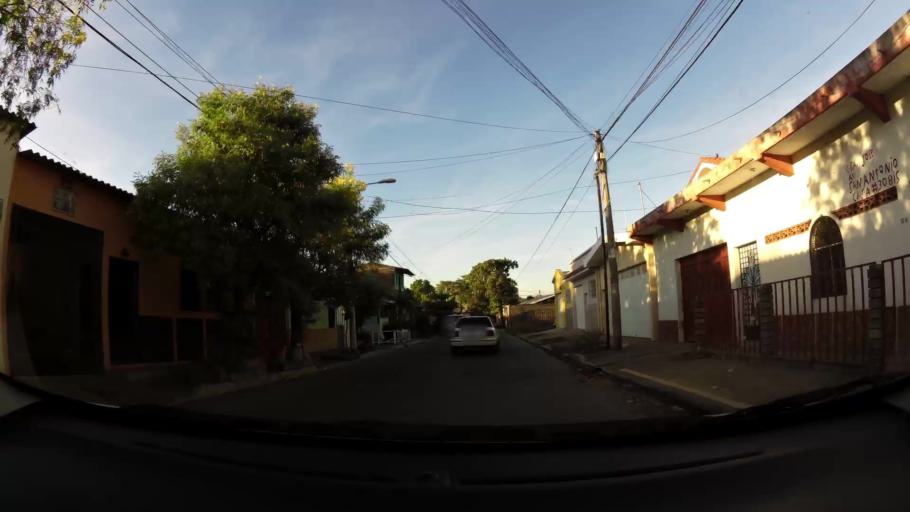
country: SV
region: San Miguel
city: San Miguel
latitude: 13.4670
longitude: -88.1689
